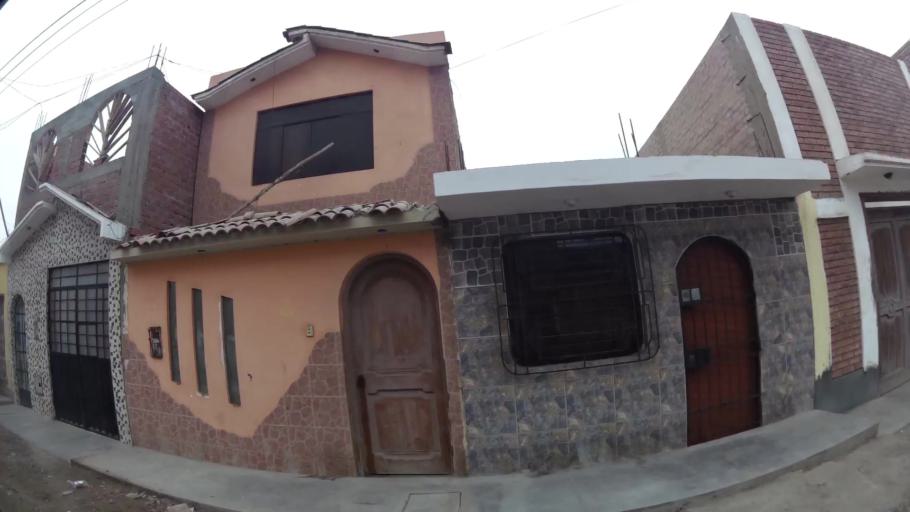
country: PE
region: Ica
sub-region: Provincia de Pisco
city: Pisco
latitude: -13.7192
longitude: -76.2133
